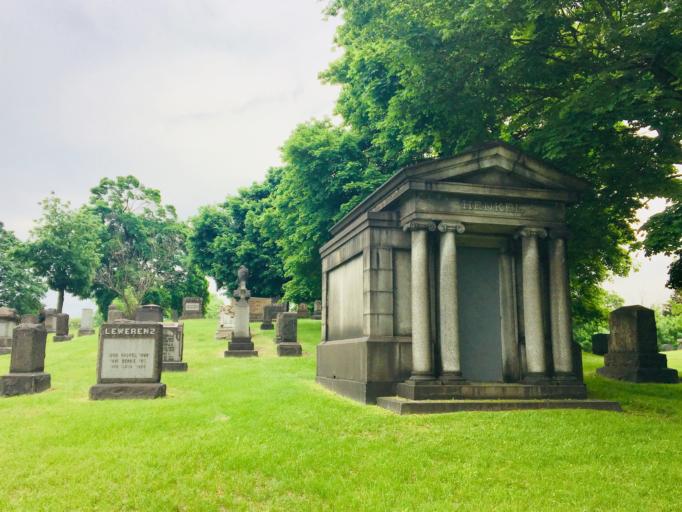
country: US
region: Michigan
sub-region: Wayne County
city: River Rouge
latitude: 42.2949
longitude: -83.1371
